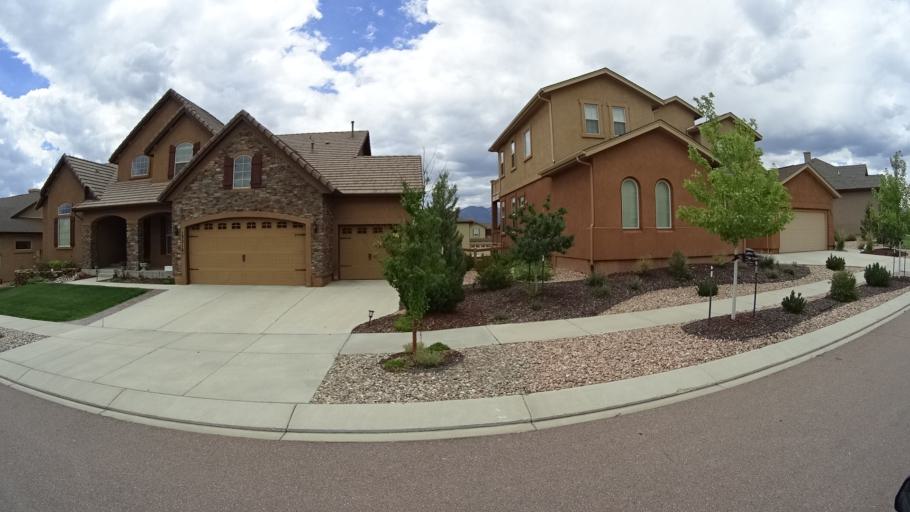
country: US
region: Colorado
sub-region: El Paso County
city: Gleneagle
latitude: 39.0215
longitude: -104.8018
